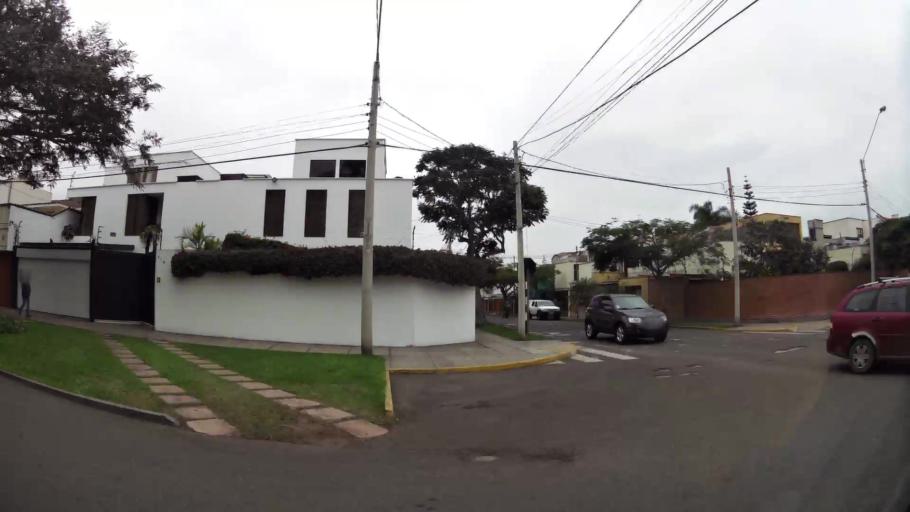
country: PE
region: Lima
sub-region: Lima
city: Surco
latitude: -12.1193
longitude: -77.0147
